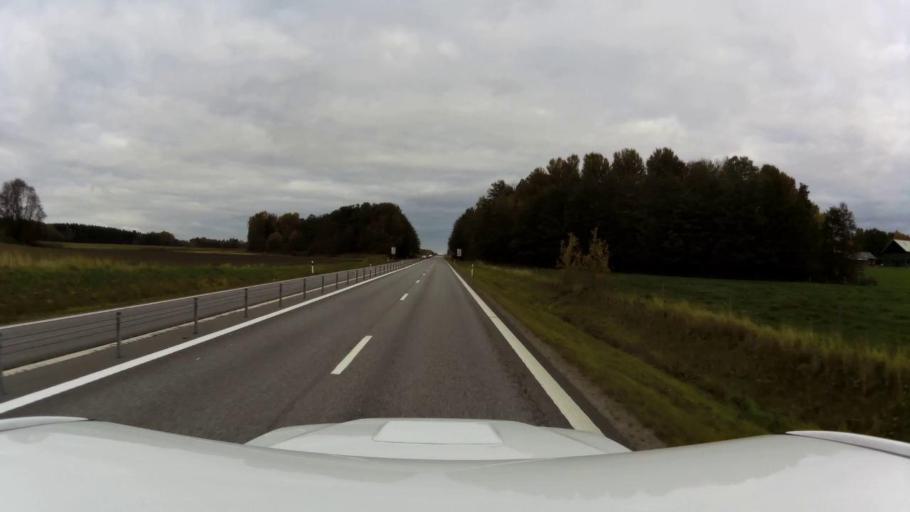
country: SE
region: OEstergoetland
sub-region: Linkopings Kommun
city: Ljungsbro
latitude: 58.4842
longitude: 15.4800
